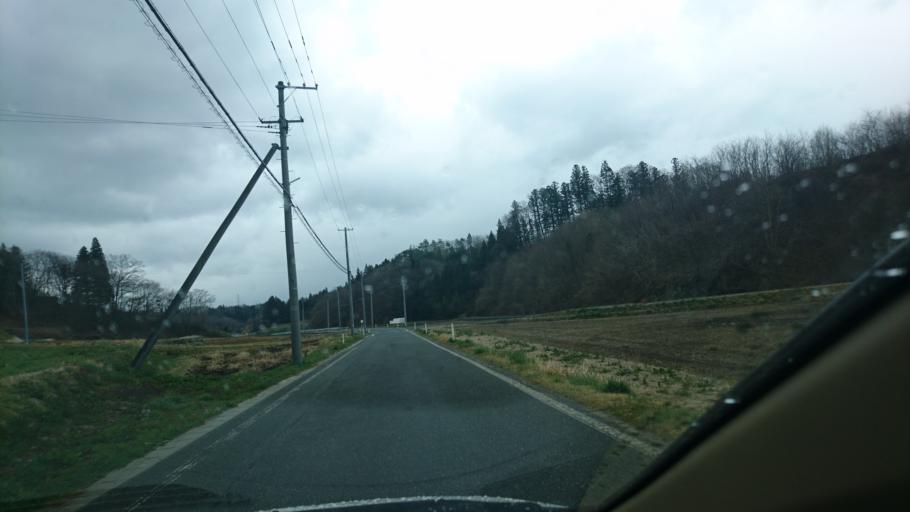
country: JP
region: Iwate
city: Ichinoseki
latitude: 38.9548
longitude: 141.3244
